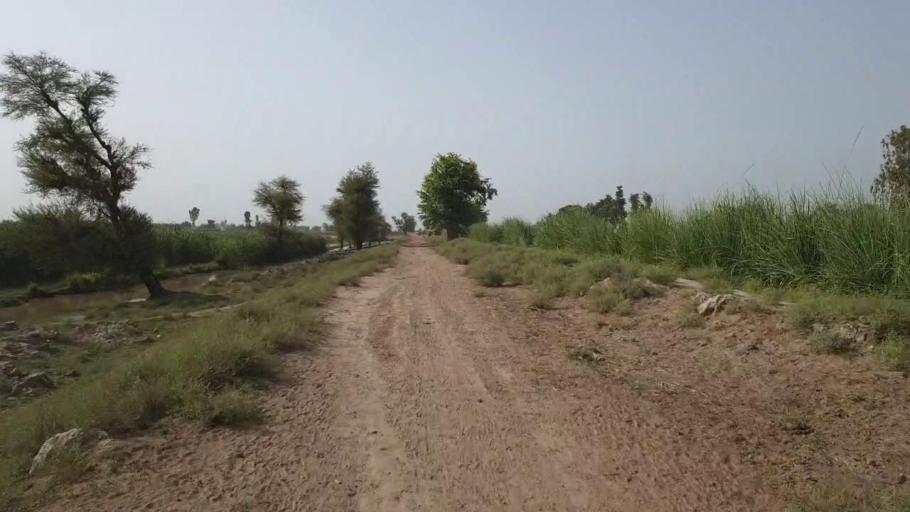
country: PK
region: Sindh
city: Daur
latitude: 26.4540
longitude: 68.1587
